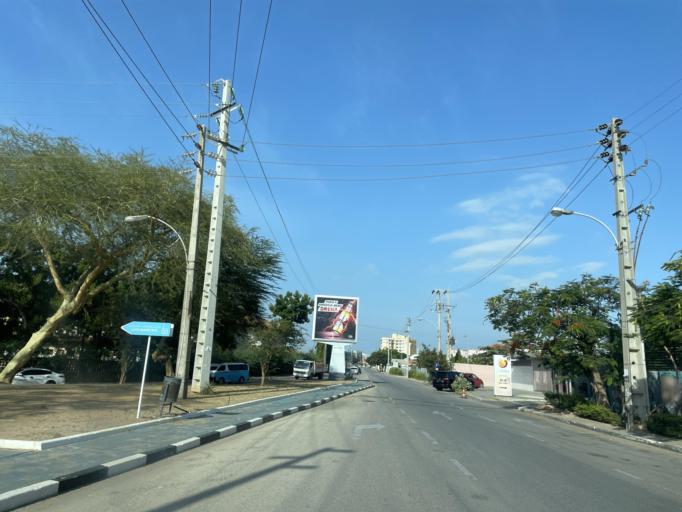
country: AO
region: Luanda
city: Luanda
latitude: -8.9156
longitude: 13.1864
